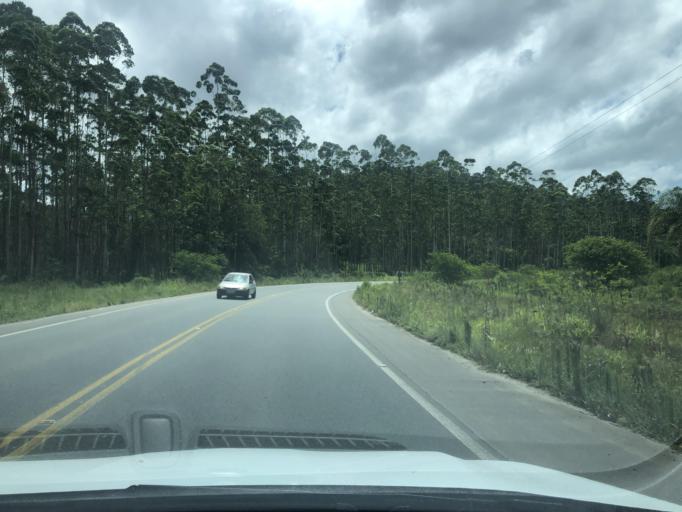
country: BR
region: Santa Catarina
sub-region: Joinville
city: Joinville
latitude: -26.3922
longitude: -48.7674
